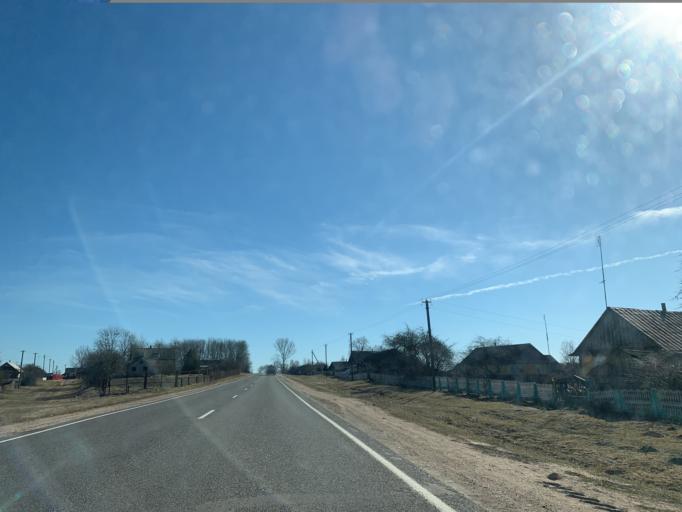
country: BY
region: Minsk
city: Nyasvizh
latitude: 53.2278
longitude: 26.7484
